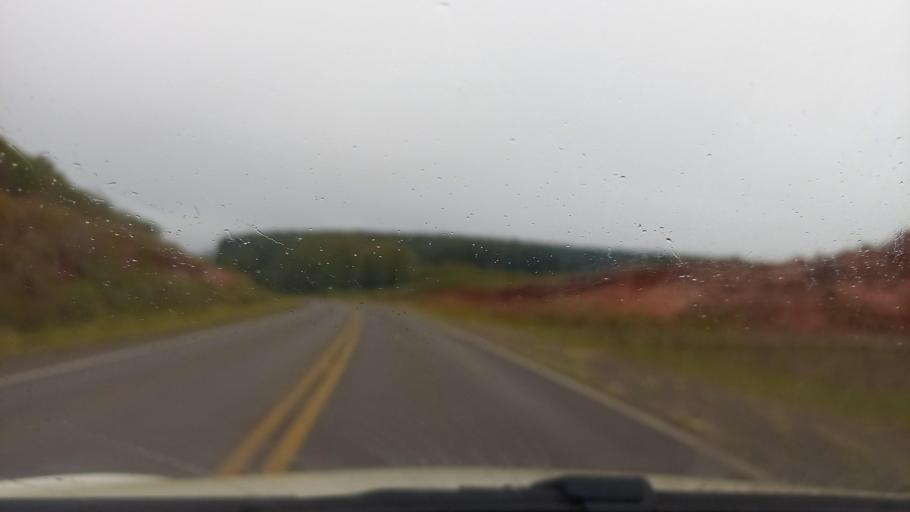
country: BR
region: Rio Grande do Sul
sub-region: Rosario Do Sul
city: Rosario do Sul
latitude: -30.1711
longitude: -54.6929
